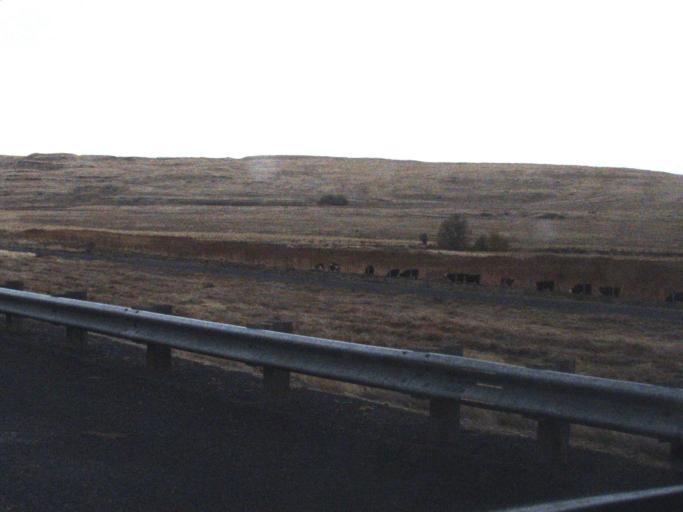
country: US
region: Washington
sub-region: Adams County
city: Ritzville
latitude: 46.7783
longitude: -118.0825
